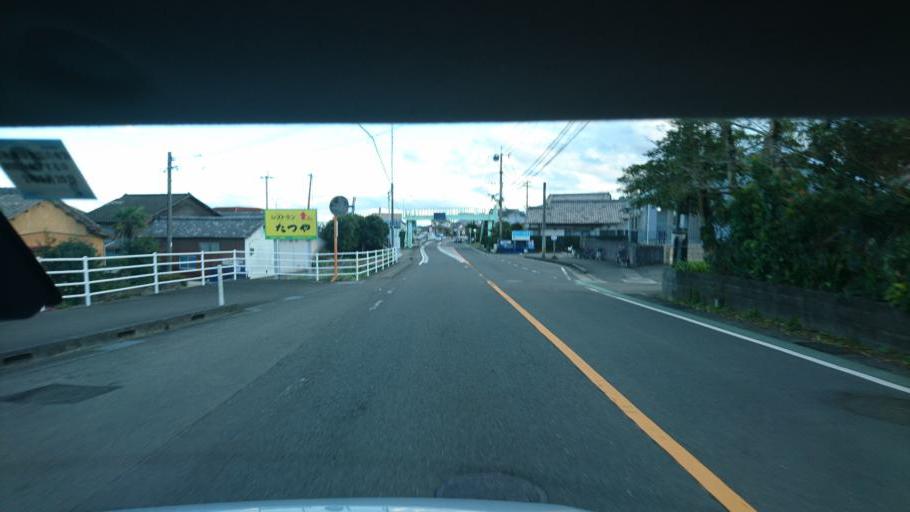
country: JP
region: Miyazaki
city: Miyazaki-shi
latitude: 31.8588
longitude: 131.4339
